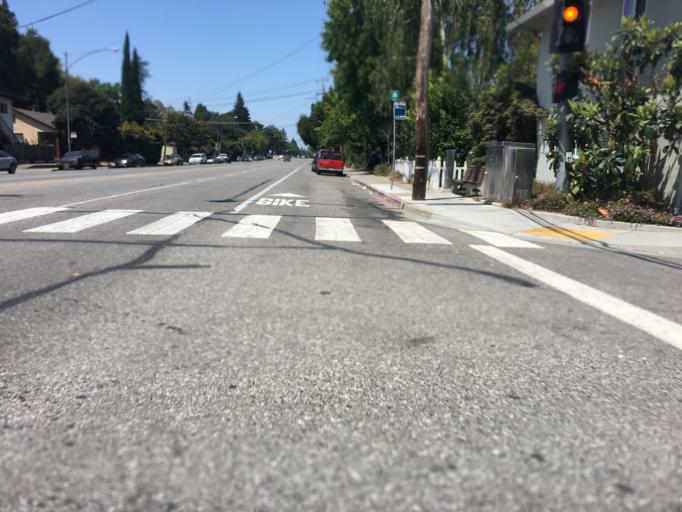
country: US
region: California
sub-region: Santa Clara County
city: Mountain View
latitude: 37.3949
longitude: -122.0894
